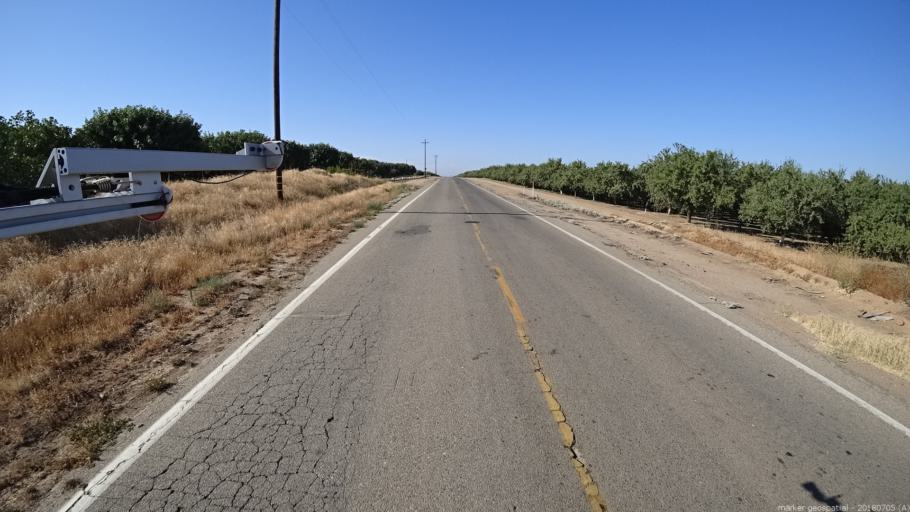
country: US
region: California
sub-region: Madera County
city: Madera Acres
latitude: 37.0963
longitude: -120.0746
